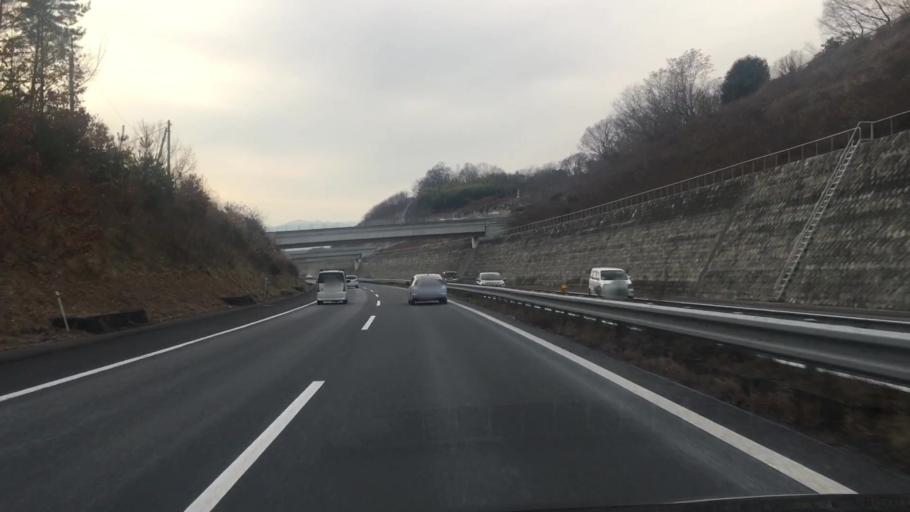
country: JP
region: Nagano
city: Ueda
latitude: 36.4097
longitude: 138.3012
